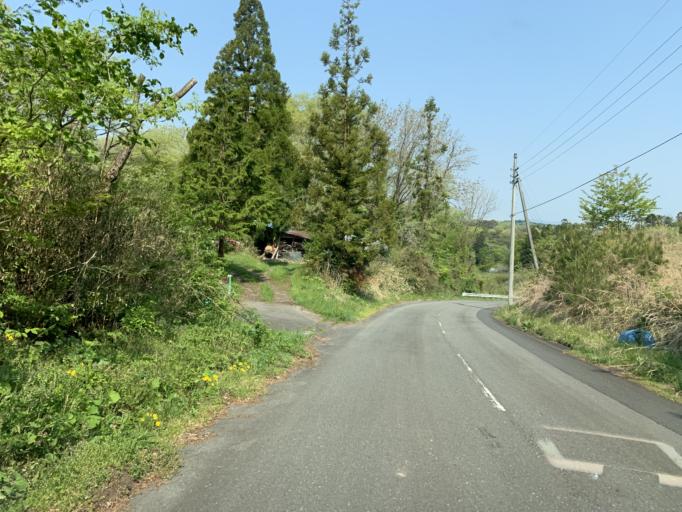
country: JP
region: Iwate
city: Ichinoseki
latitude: 38.8918
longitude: 141.0632
